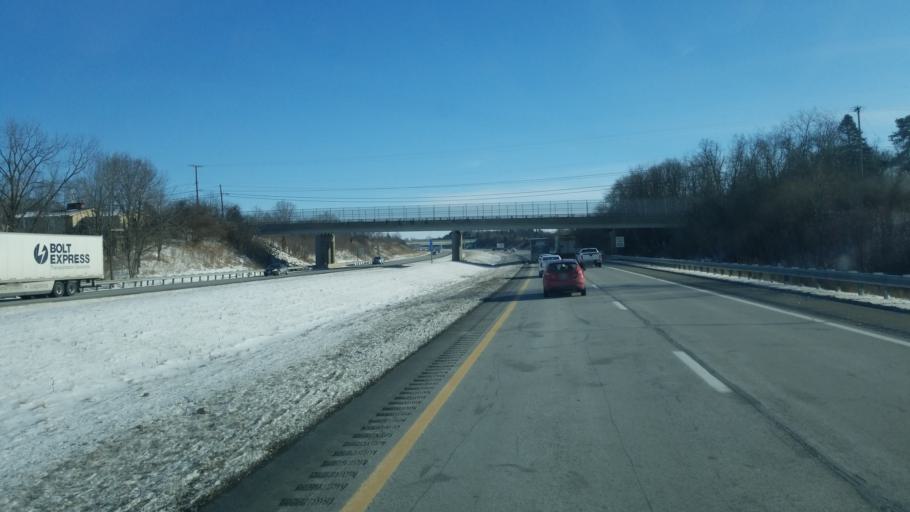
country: US
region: Ohio
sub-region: Lucas County
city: Maumee
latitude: 41.5419
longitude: -83.6805
